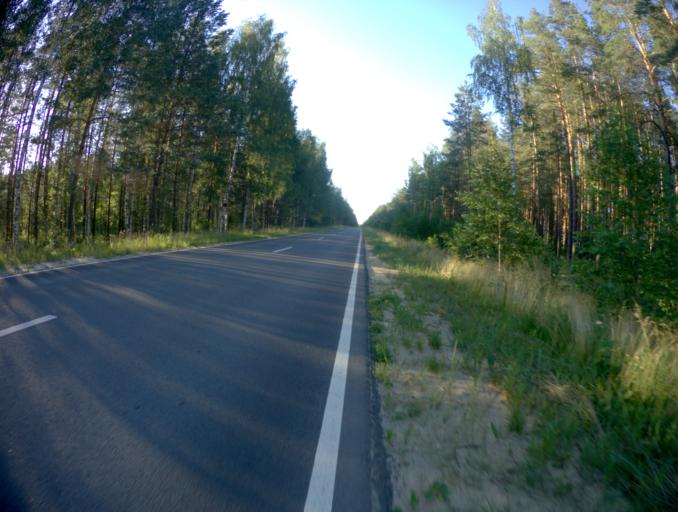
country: RU
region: Vladimir
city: Galitsy
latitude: 56.1126
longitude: 42.8717
